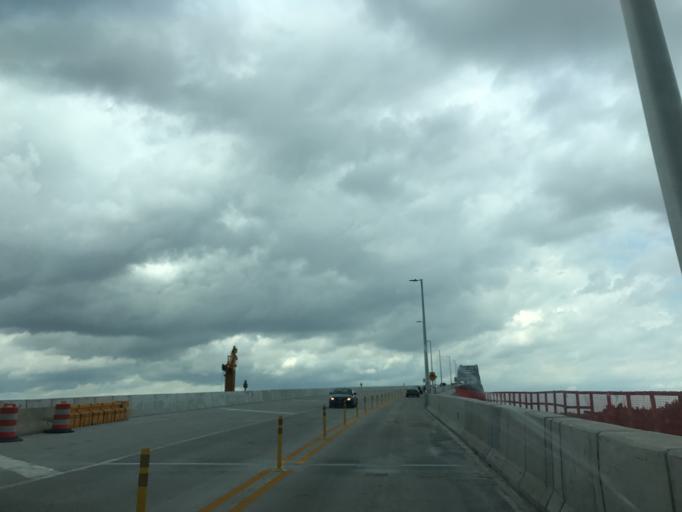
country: US
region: New York
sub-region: Richmond County
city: Bloomfield
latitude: 40.6340
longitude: -74.1451
